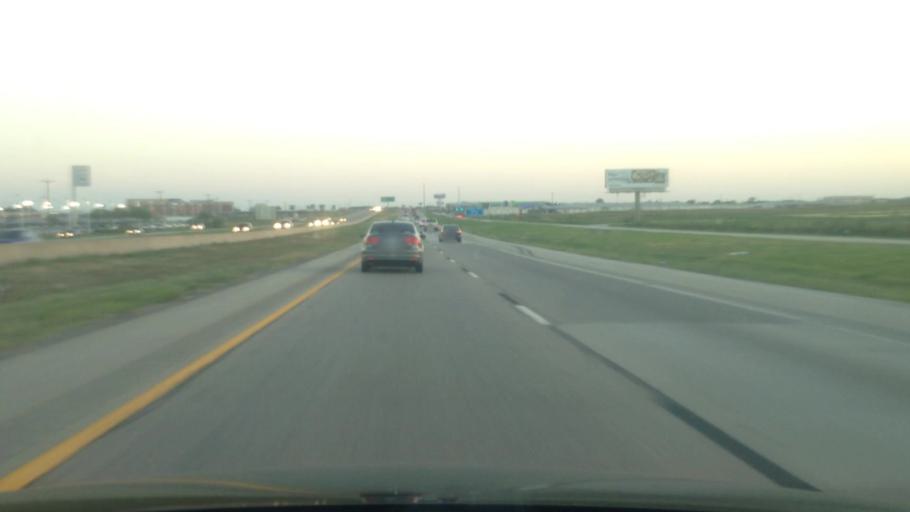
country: US
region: Texas
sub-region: Tarrant County
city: Haslet
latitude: 32.9390
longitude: -97.3138
